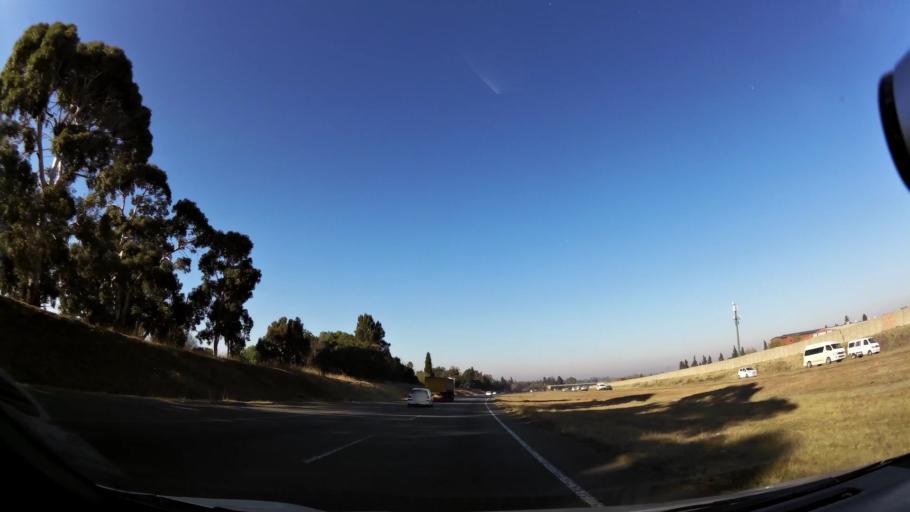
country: ZA
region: Gauteng
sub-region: Ekurhuleni Metropolitan Municipality
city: Germiston
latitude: -26.3253
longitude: 28.1127
